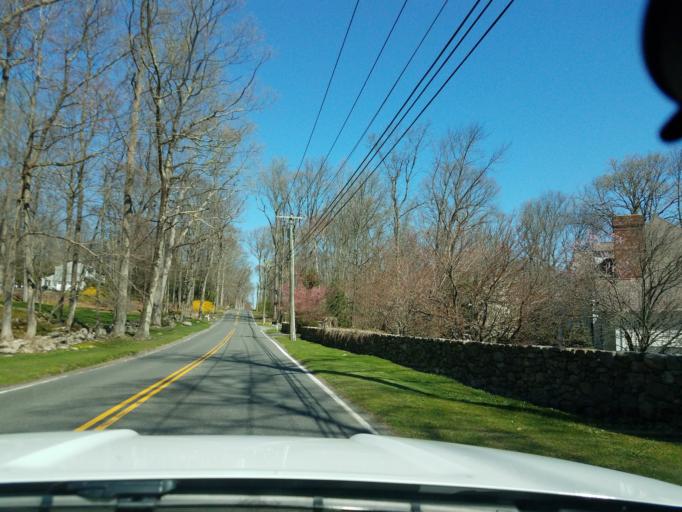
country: US
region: Connecticut
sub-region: Fairfield County
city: Wilton
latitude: 41.2106
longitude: -73.3731
